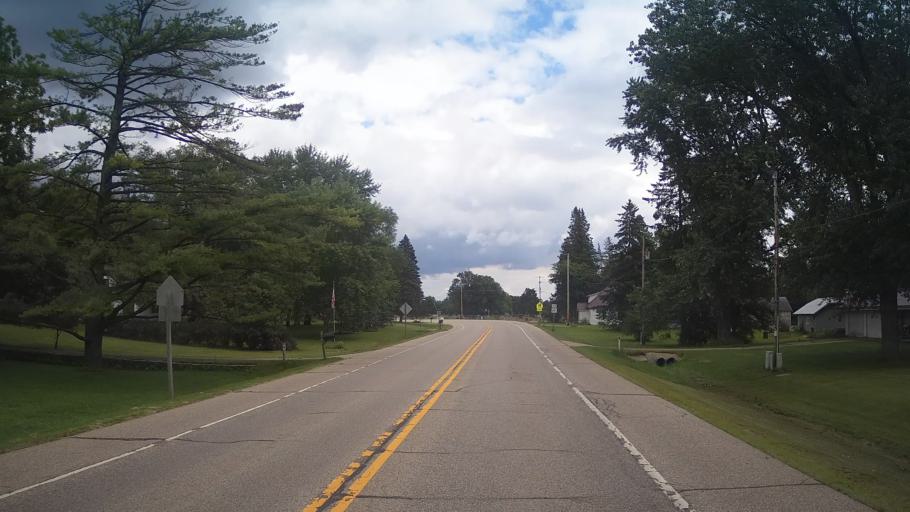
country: US
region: Wisconsin
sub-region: Marquette County
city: Westfield
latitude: 44.0355
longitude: -89.5200
